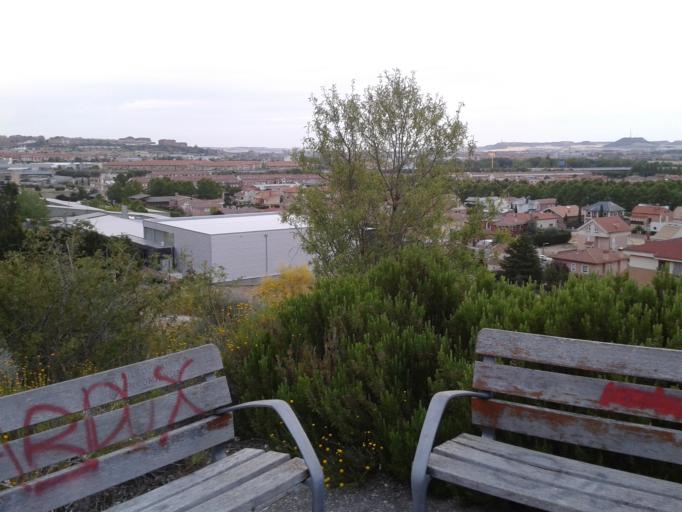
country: ES
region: Castille and Leon
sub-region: Provincia de Valladolid
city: Arroyo
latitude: 41.6151
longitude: -4.7864
